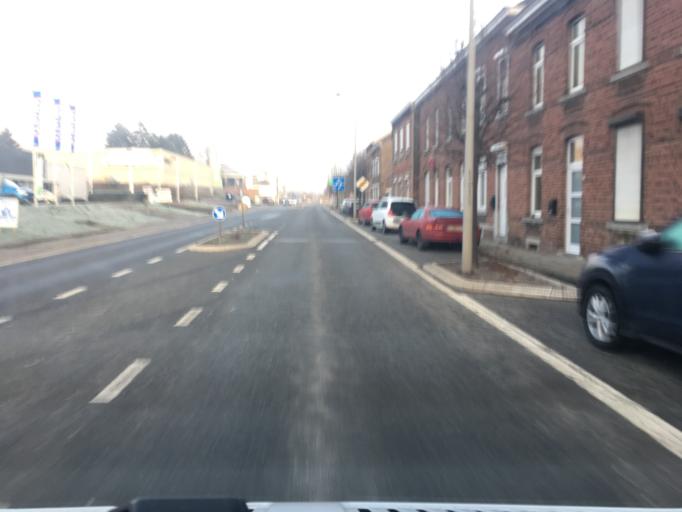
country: BE
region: Wallonia
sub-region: Province de Liege
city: Huy
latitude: 50.5217
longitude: 5.2201
